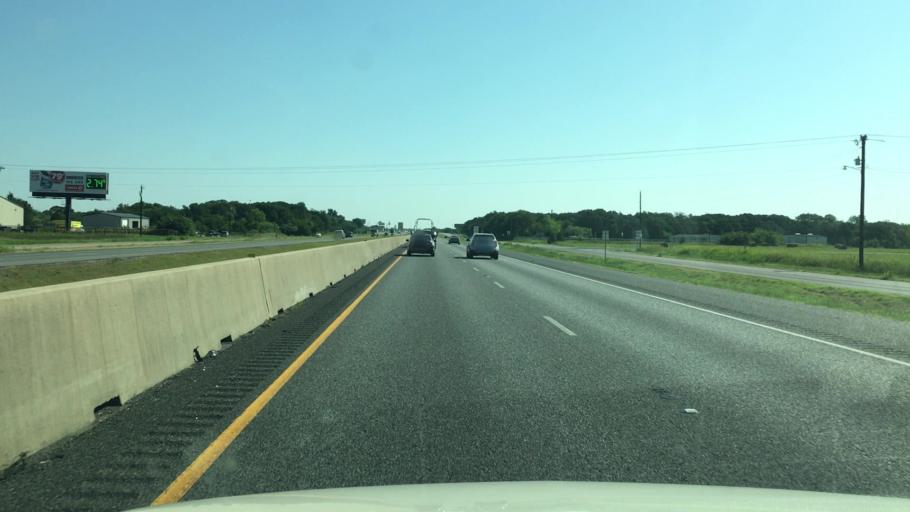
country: US
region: Texas
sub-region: Hunt County
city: Caddo Mills
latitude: 33.0240
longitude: -96.1978
